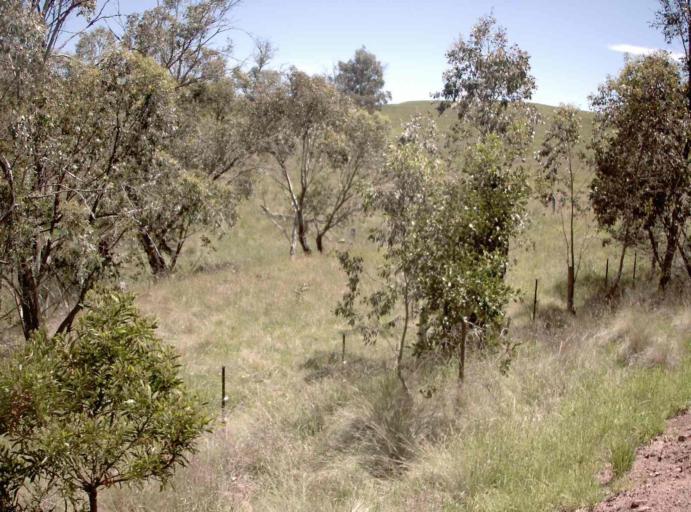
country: AU
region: New South Wales
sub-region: Snowy River
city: Jindabyne
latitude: -37.1036
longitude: 148.2503
